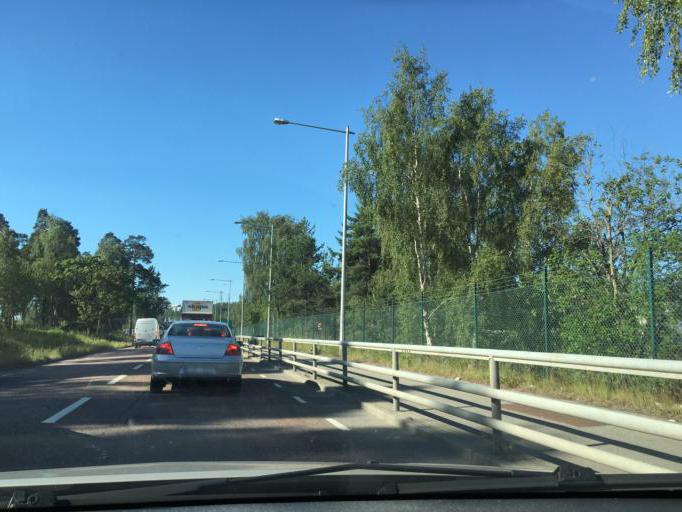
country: SE
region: Stockholm
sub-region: Sodertalje Kommun
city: Soedertaelje
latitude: 59.1804
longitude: 17.6405
